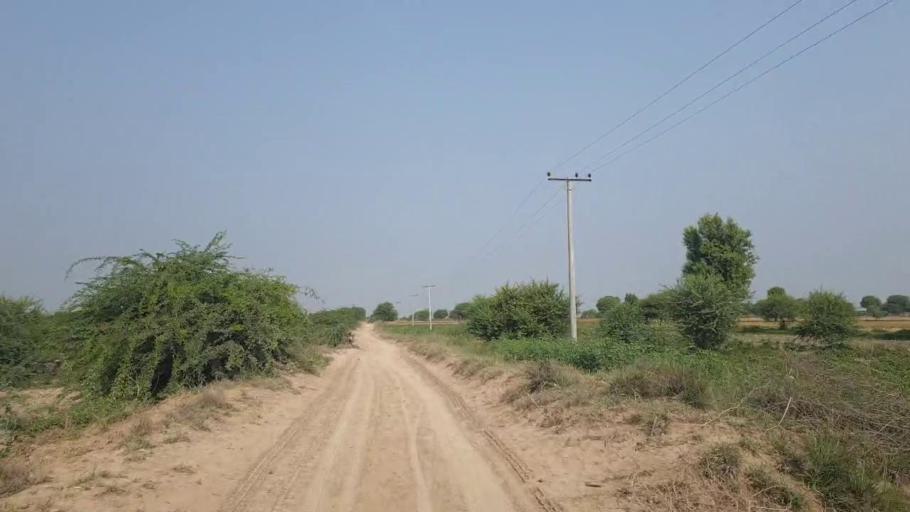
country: PK
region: Sindh
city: Badin
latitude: 24.6969
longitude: 68.7782
